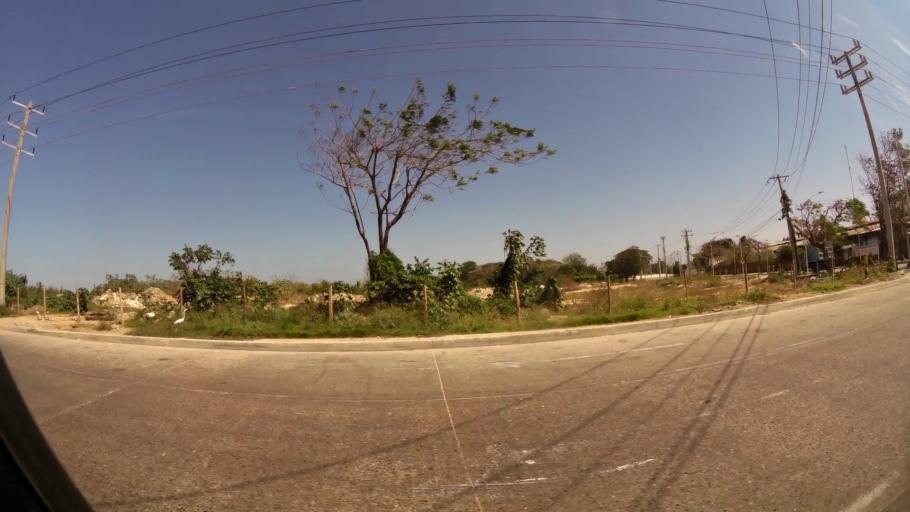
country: CO
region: Atlantico
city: Barranquilla
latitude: 10.9748
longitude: -74.7688
